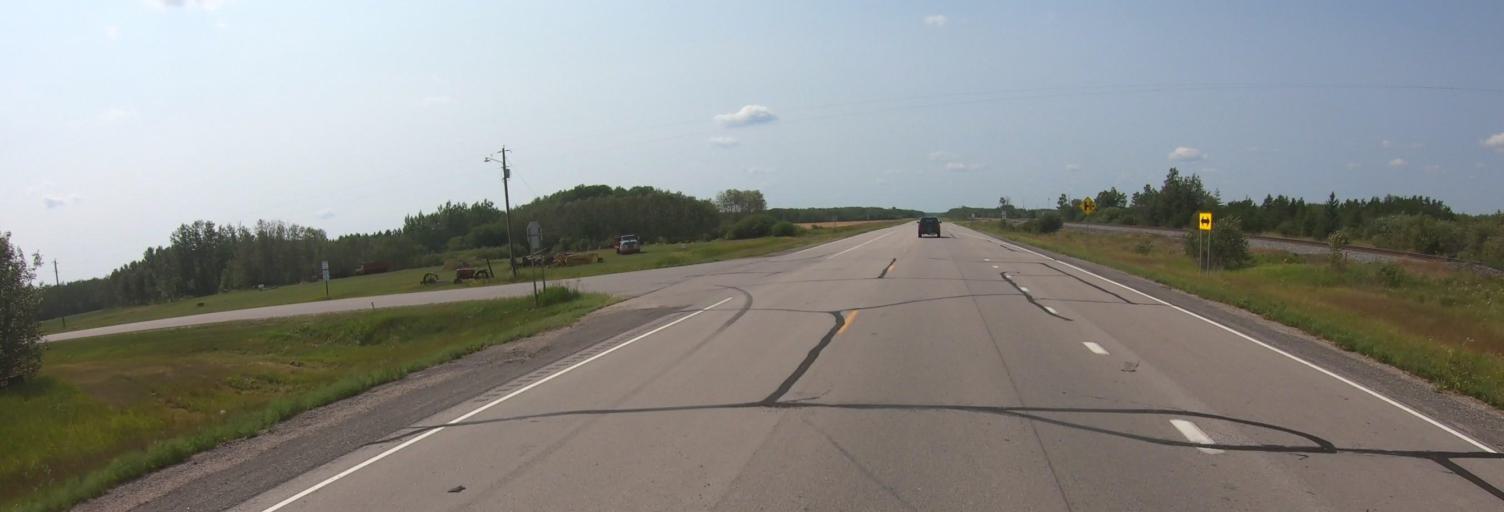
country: US
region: Minnesota
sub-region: Lake of the Woods County
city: Baudette
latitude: 48.7133
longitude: -94.6485
